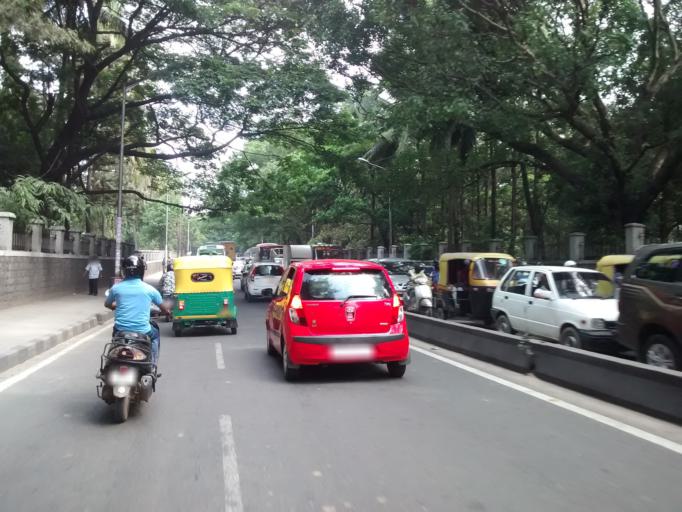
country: IN
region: Karnataka
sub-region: Bangalore Urban
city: Bangalore
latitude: 12.9419
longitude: 77.5975
